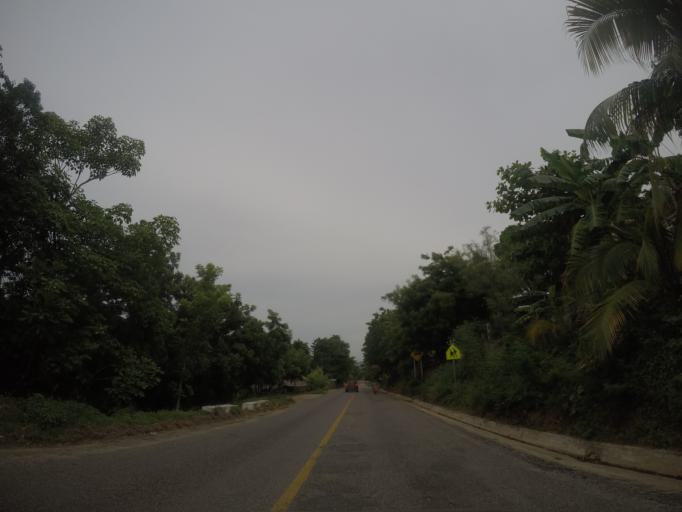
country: MX
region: Oaxaca
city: San Pedro Mixtepec
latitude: 15.9471
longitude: -97.1869
